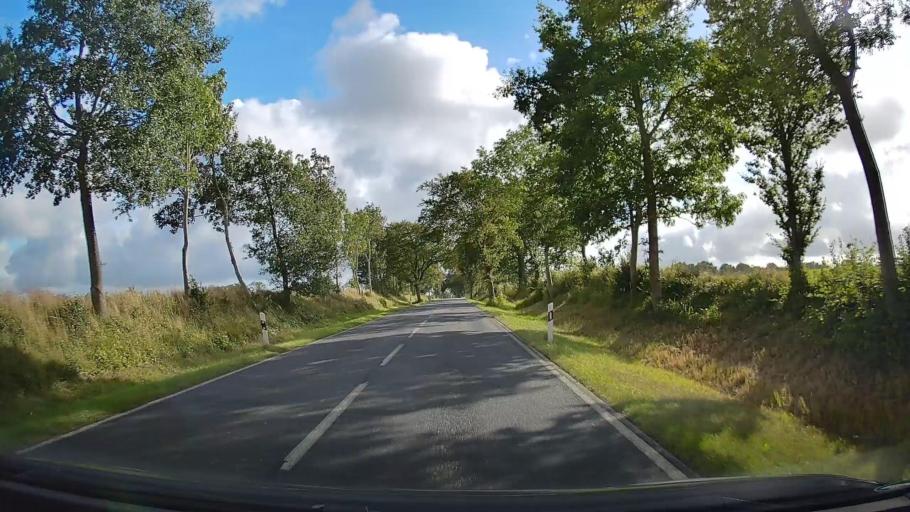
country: DE
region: Mecklenburg-Vorpommern
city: Putbus
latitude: 54.3710
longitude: 13.4796
